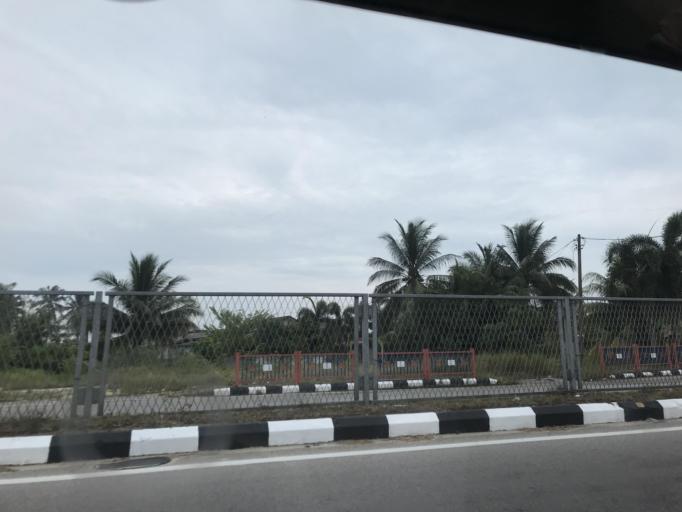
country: MY
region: Kelantan
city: Kota Bharu
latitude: 6.1188
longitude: 102.2158
